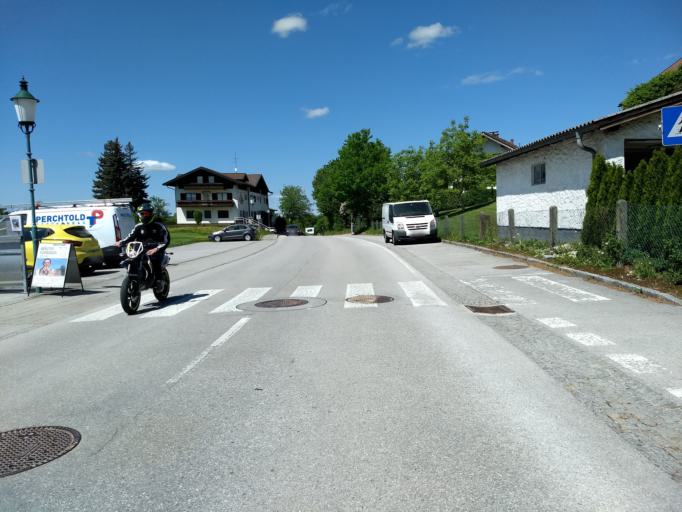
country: AT
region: Salzburg
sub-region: Politischer Bezirk Salzburg-Umgebung
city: Bergheim
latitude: 47.8363
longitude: 13.0269
